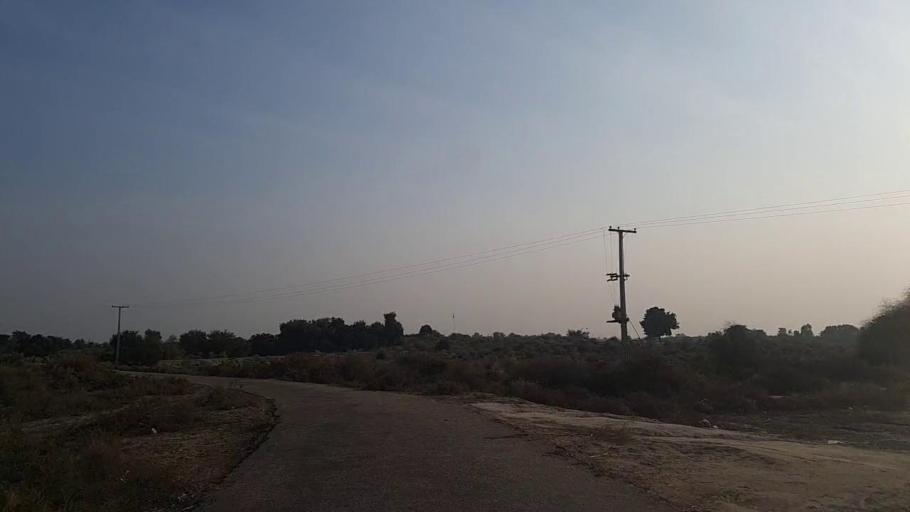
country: PK
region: Sindh
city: Jam Sahib
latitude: 26.4341
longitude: 68.5932
